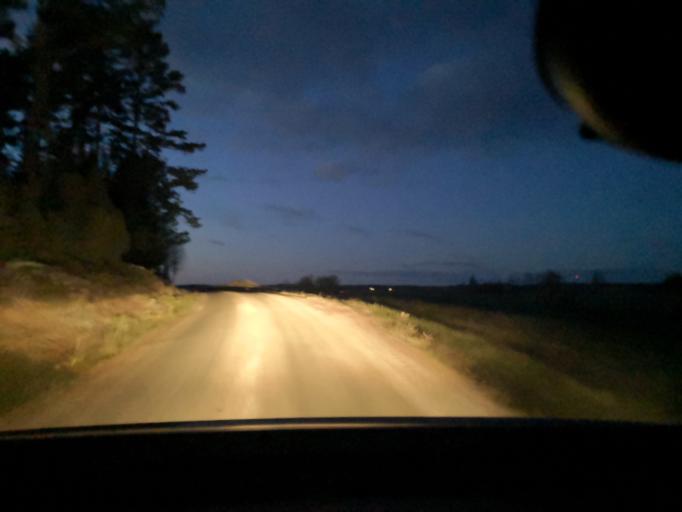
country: SE
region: Uppsala
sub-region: Heby Kommun
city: Heby
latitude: 59.9144
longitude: 16.7512
